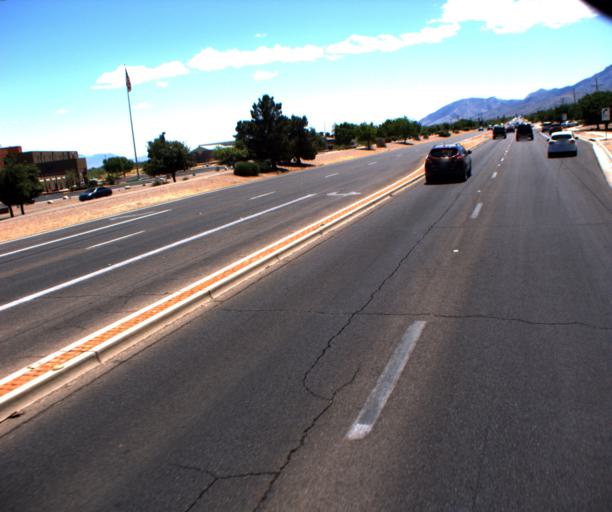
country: US
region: Arizona
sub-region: Cochise County
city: Sierra Vista
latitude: 31.5322
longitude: -110.2574
